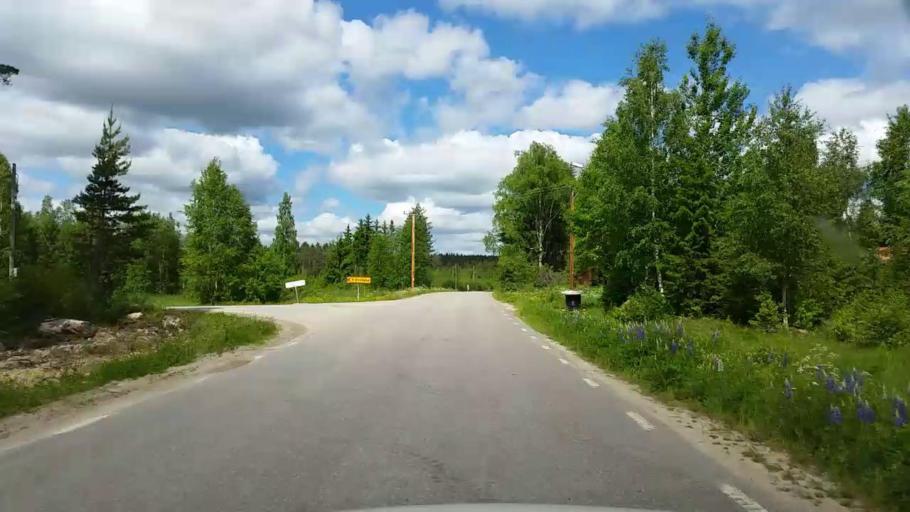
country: SE
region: Gaevleborg
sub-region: Ovanakers Kommun
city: Alfta
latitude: 61.4018
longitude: 16.0496
